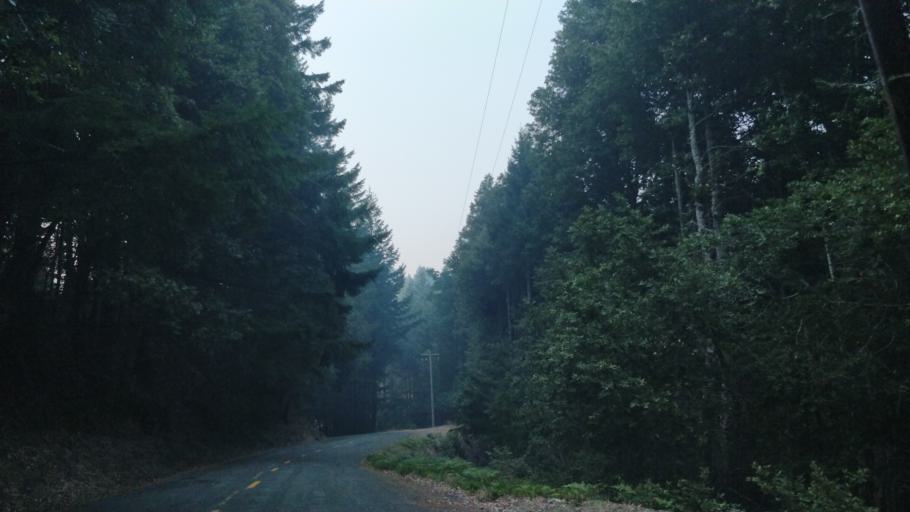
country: US
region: California
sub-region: Humboldt County
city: Rio Dell
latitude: 40.3031
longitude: -124.0607
